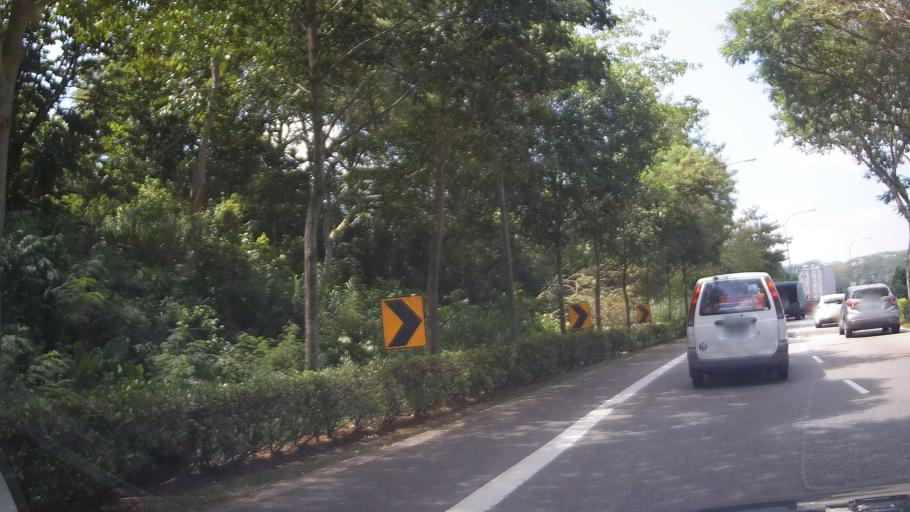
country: MY
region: Johor
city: Johor Bahru
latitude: 1.4210
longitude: 103.7727
